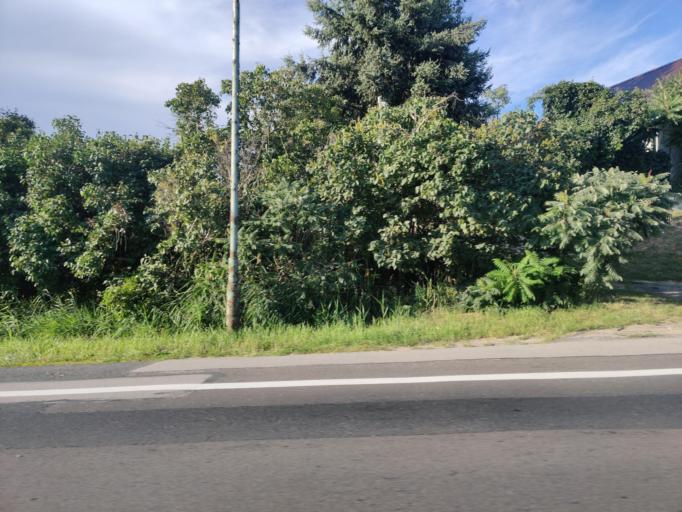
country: PL
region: Greater Poland Voivodeship
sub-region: Konin
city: Konin
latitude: 52.2014
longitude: 18.2803
